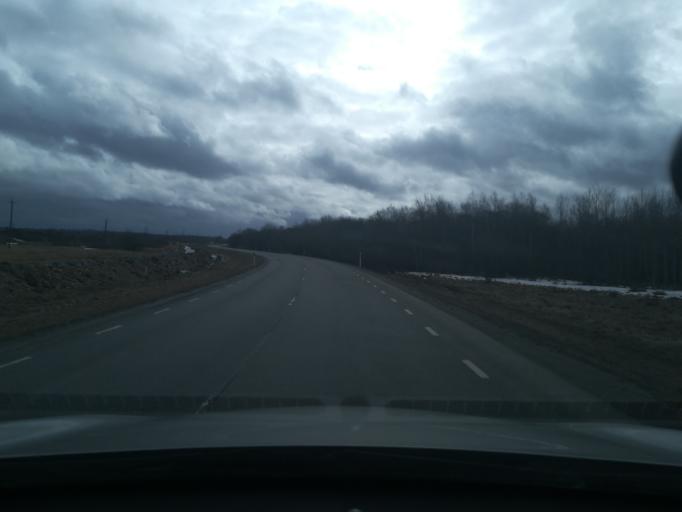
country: EE
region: Harju
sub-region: Harku vald
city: Tabasalu
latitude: 59.4009
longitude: 24.5483
